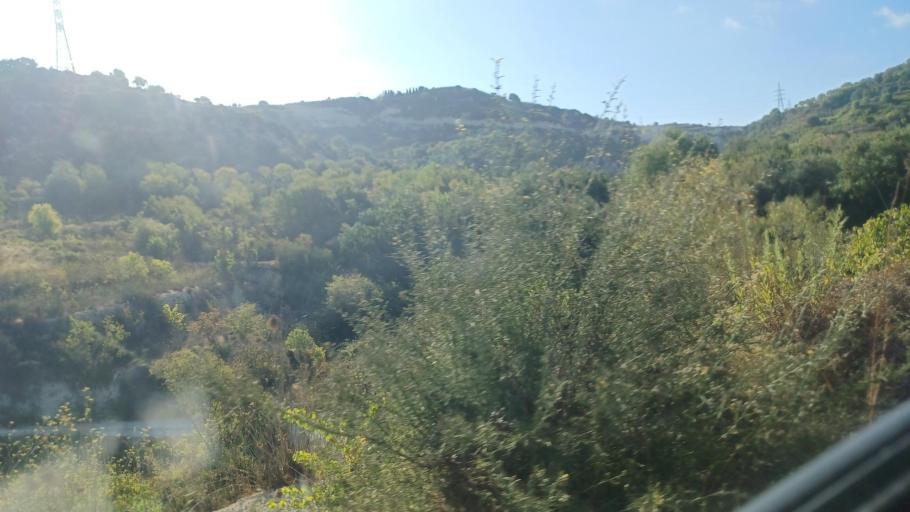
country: CY
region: Pafos
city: Mesogi
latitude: 34.8454
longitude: 32.4818
